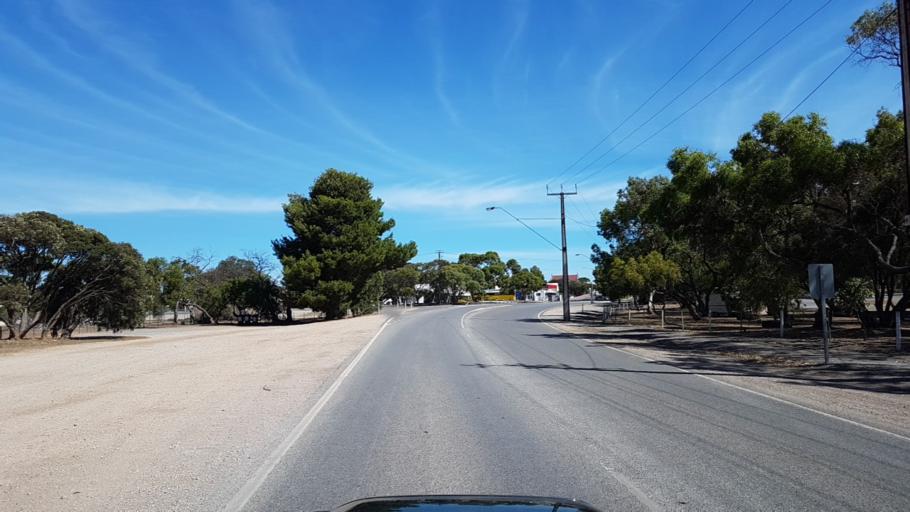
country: AU
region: South Australia
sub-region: Yorke Peninsula
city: Port Victoria
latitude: -34.7660
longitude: 137.5978
